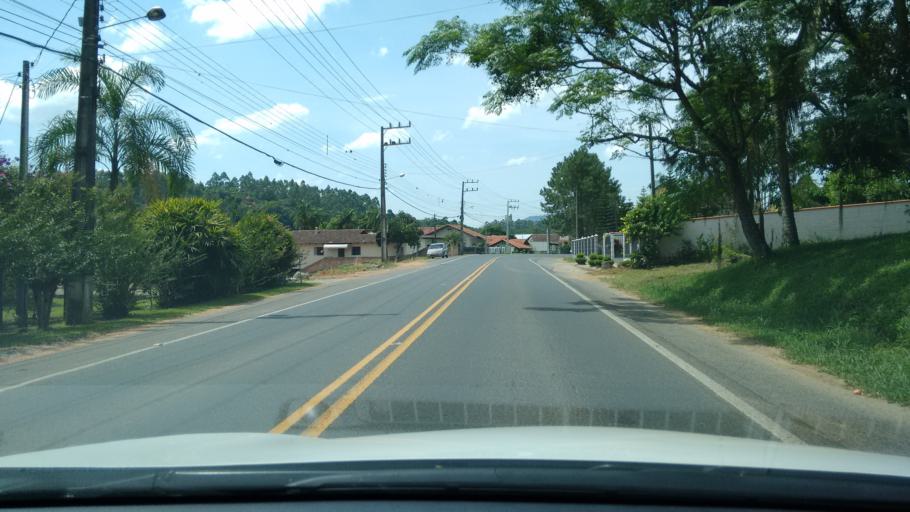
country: BR
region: Santa Catarina
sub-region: Timbo
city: Timbo
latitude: -26.8288
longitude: -49.2990
